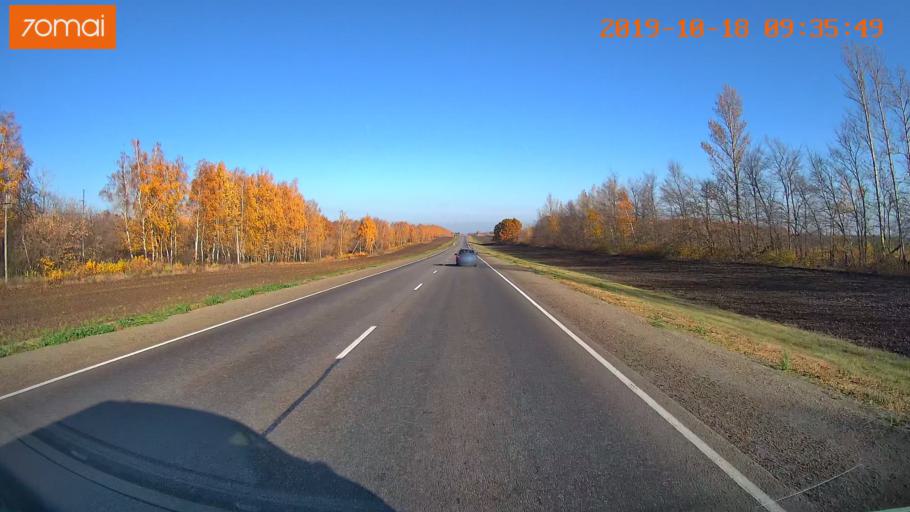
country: RU
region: Tula
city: Yefremov
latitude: 53.1973
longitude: 38.1473
